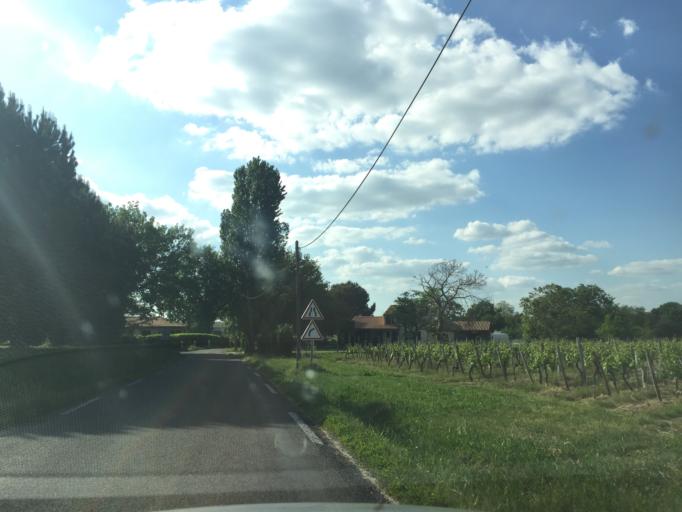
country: FR
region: Aquitaine
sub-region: Departement de la Gironde
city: Saint-Denis-de-Pile
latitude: 44.9576
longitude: -0.2080
